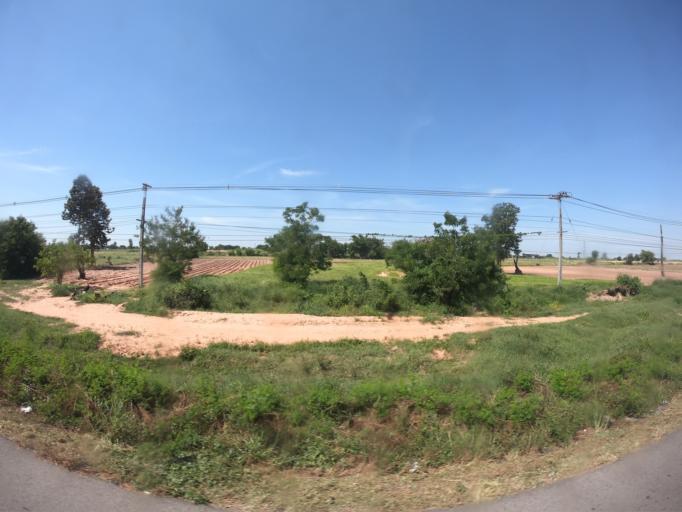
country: TH
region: Khon Kaen
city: Non Sila
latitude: 15.9345
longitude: 102.6728
